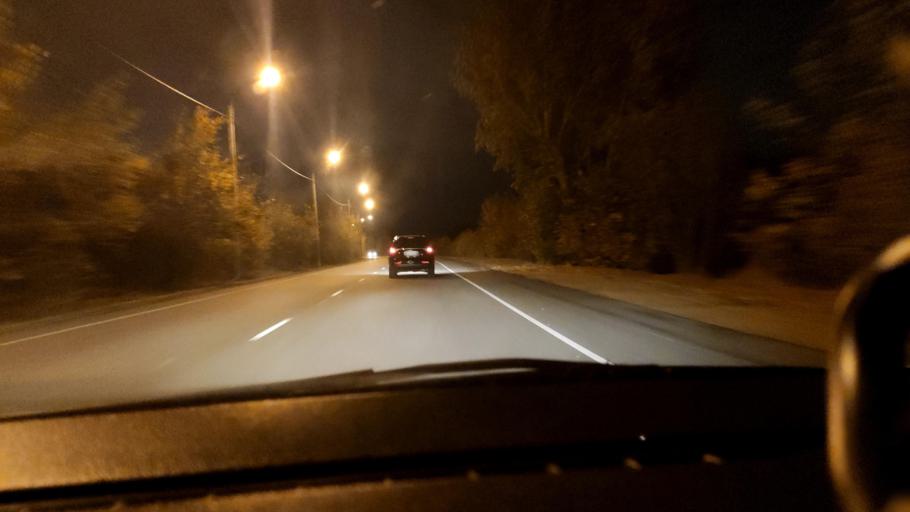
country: RU
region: Voronezj
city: Voronezh
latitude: 51.6072
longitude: 39.1792
